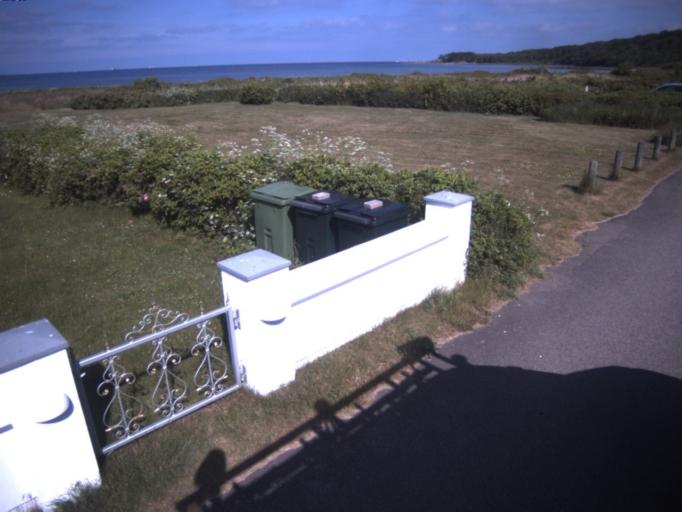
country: DK
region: Capital Region
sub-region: Helsingor Kommune
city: Helsingor
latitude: 56.0997
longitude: 12.6320
